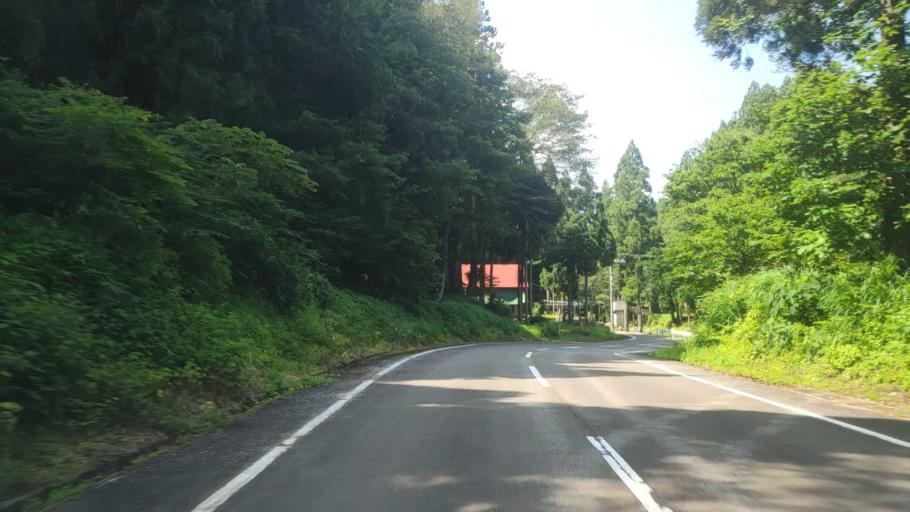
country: JP
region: Ishikawa
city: Komatsu
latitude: 36.2487
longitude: 136.5378
